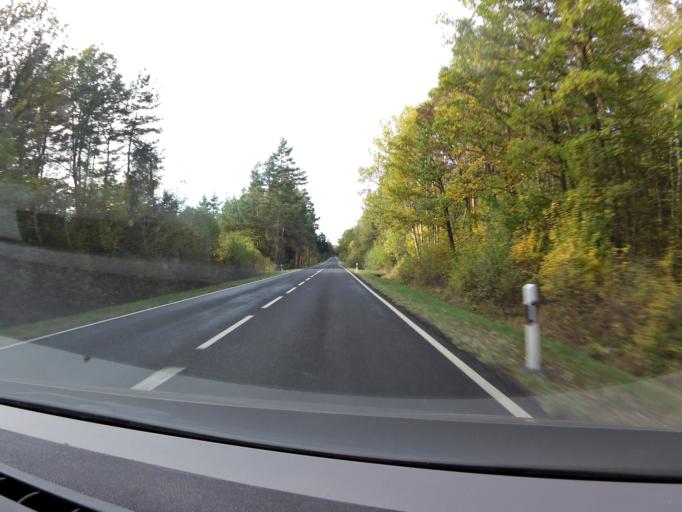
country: DE
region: Thuringia
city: Crawinkel
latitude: 50.7883
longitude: 10.7627
